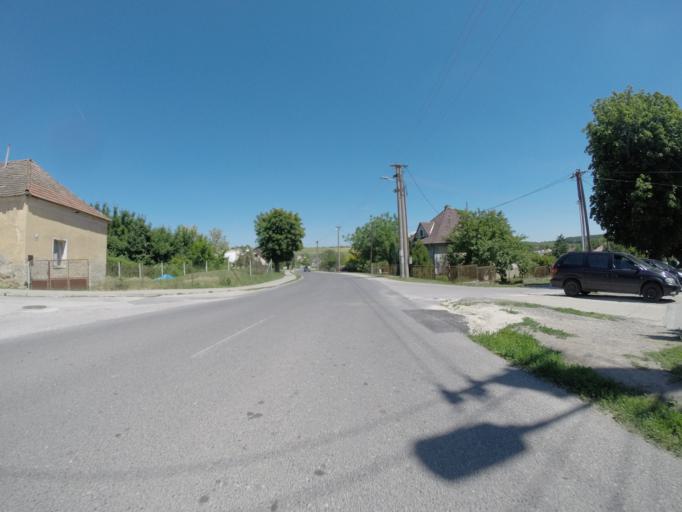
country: SK
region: Trnavsky
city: Hlohovec
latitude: 48.4899
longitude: 17.8779
